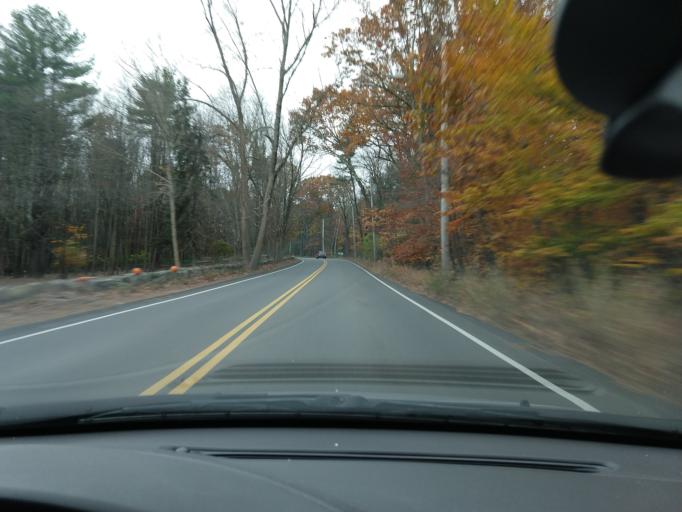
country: US
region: Massachusetts
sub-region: Middlesex County
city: Carlisle
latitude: 42.5525
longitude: -71.3533
